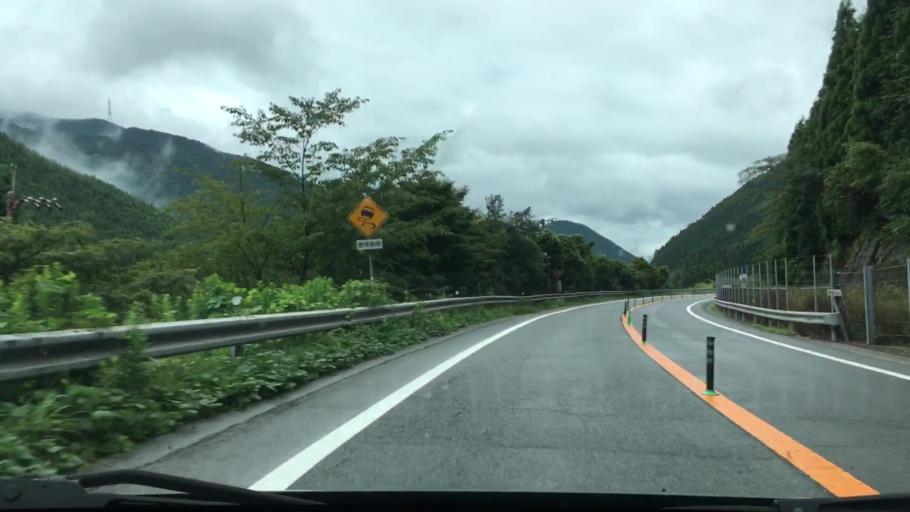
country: JP
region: Hyogo
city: Nishiwaki
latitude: 35.1378
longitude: 134.7901
